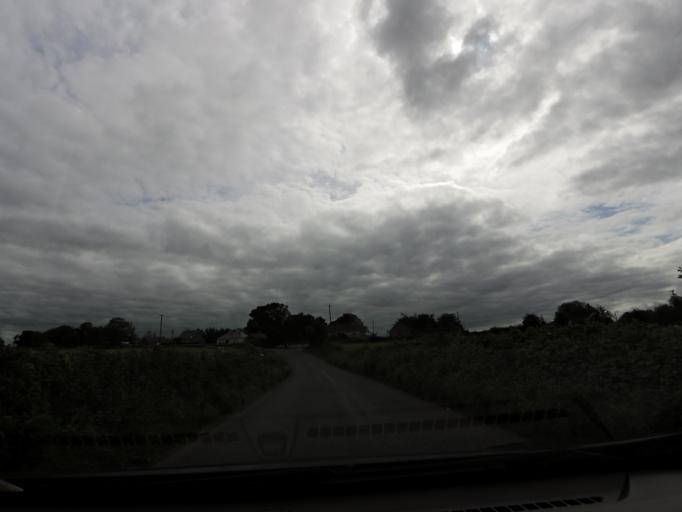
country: IE
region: Connaught
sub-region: County Galway
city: Loughrea
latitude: 53.1809
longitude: -8.4911
